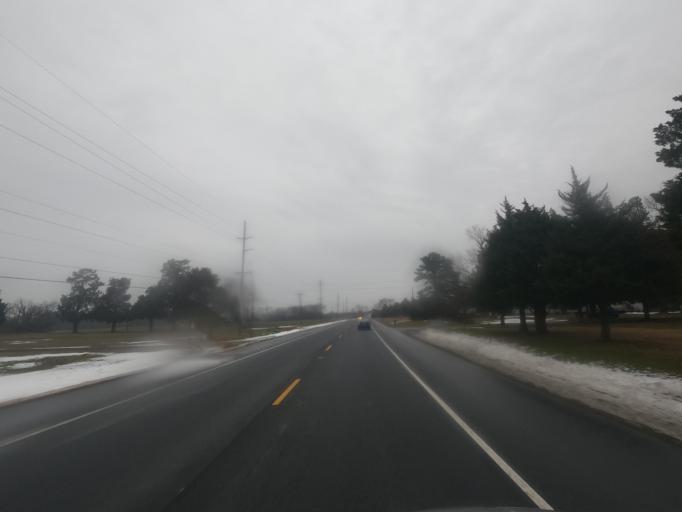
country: US
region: Maryland
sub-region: Dorchester County
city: Cambridge
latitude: 38.5808
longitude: -75.9669
